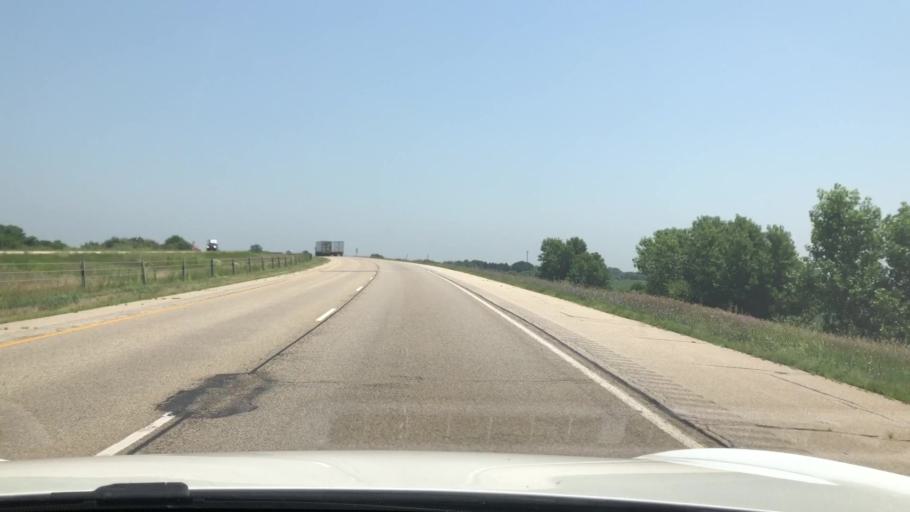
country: US
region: Illinois
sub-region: De Witt County
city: Farmer City
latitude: 40.2633
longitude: -88.6615
